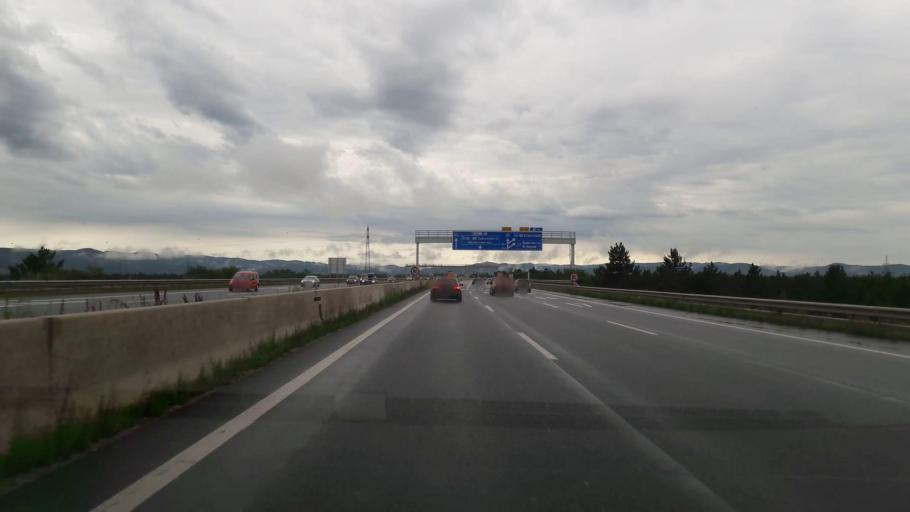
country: AT
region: Lower Austria
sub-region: Wiener Neustadt Stadt
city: Wiener Neustadt
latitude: 47.7990
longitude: 16.2018
